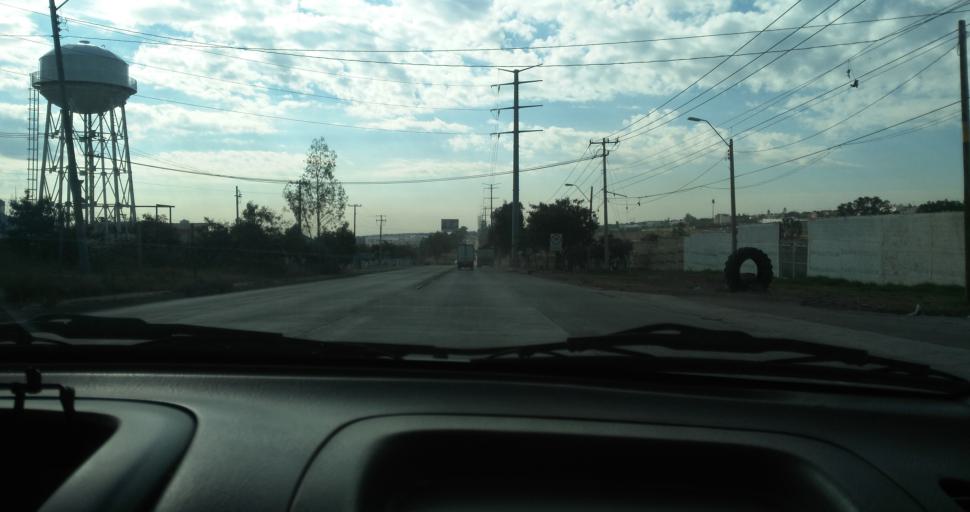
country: MX
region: Guanajuato
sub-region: Leon
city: Fraccionamiento Paseo de las Torres
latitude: 21.1758
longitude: -101.7402
